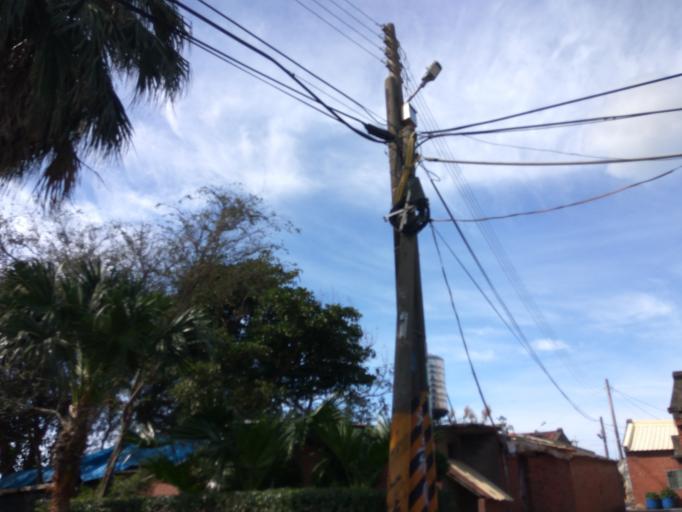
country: TW
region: Taiwan
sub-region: Hsinchu
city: Zhubei
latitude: 25.0142
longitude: 121.0796
